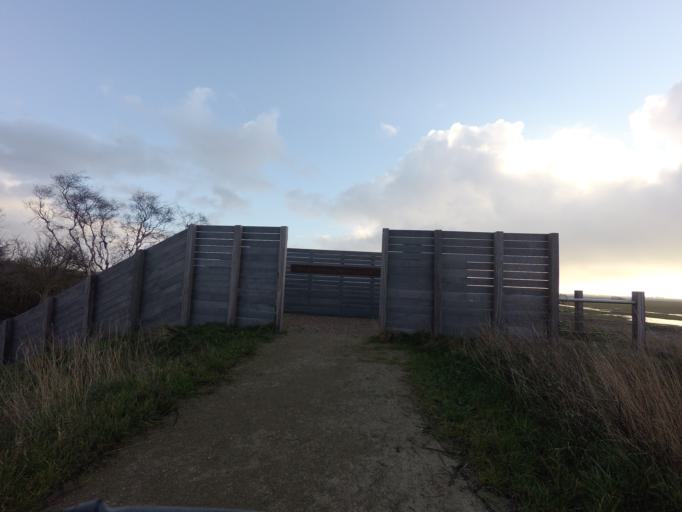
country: NL
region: North Holland
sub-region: Gemeente Texel
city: Den Burg
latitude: 53.0928
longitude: 4.8081
